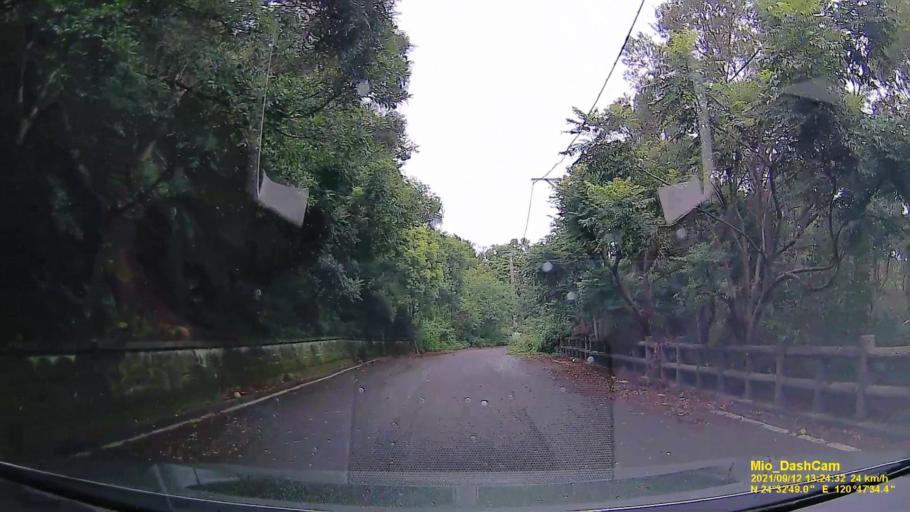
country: TW
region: Taiwan
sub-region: Miaoli
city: Miaoli
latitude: 24.5469
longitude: 120.7929
